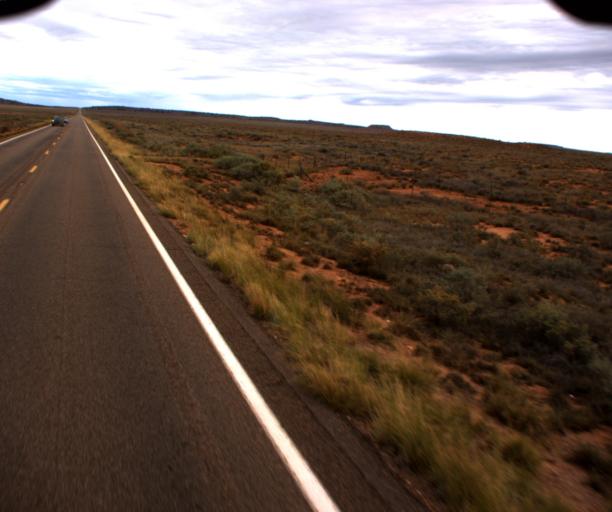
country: US
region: Arizona
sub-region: Navajo County
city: Holbrook
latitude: 34.7315
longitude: -110.1170
